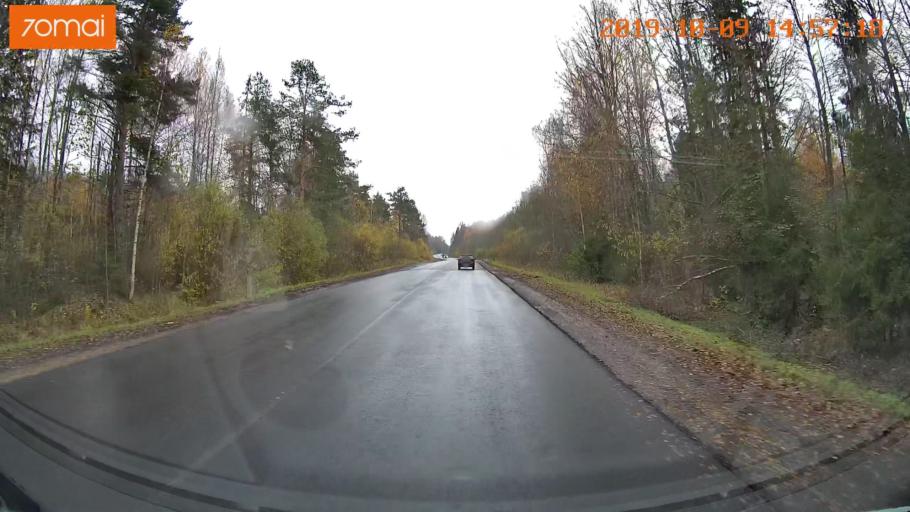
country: RU
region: Kostroma
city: Chistyye Bory
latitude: 58.3391
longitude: 41.6501
